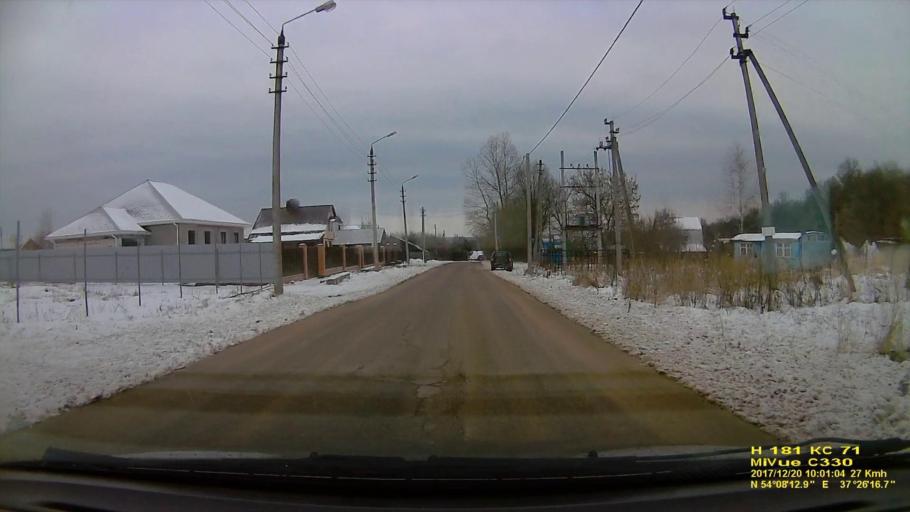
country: RU
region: Tula
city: Kosaya Gora
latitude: 54.1368
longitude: 37.4380
